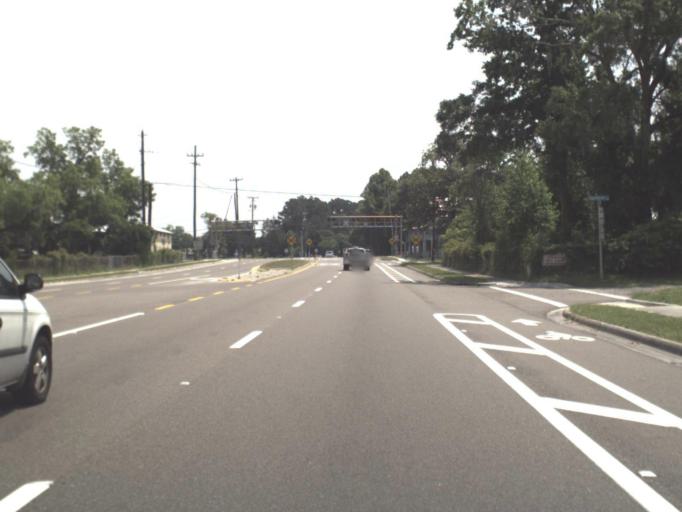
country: US
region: Florida
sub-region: Nassau County
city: Yulee
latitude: 30.6305
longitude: -81.6080
